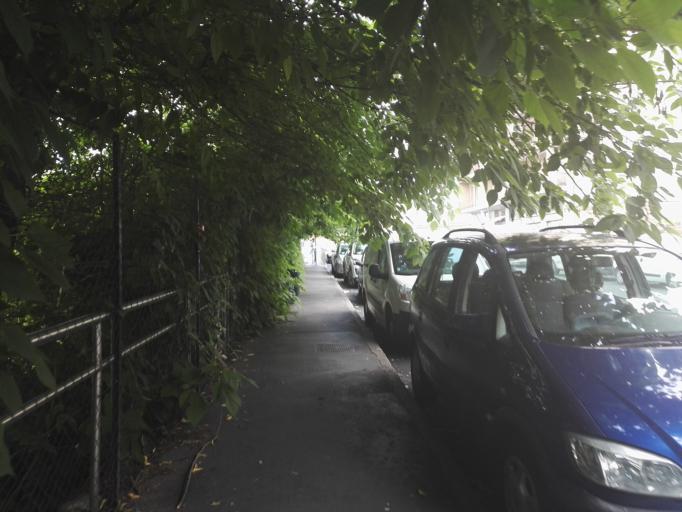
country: IT
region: Lombardy
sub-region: Citta metropolitana di Milano
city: Milano
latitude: 45.4452
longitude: 9.2120
